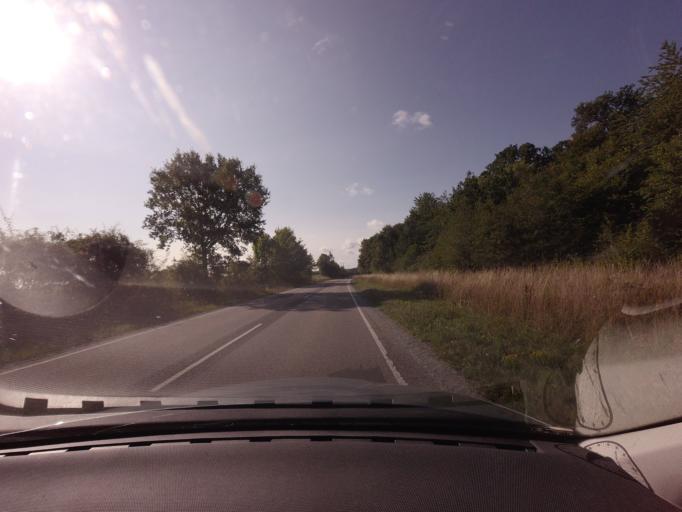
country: DK
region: Zealand
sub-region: Vordingborg Kommune
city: Praesto
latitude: 55.0373
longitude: 12.1033
